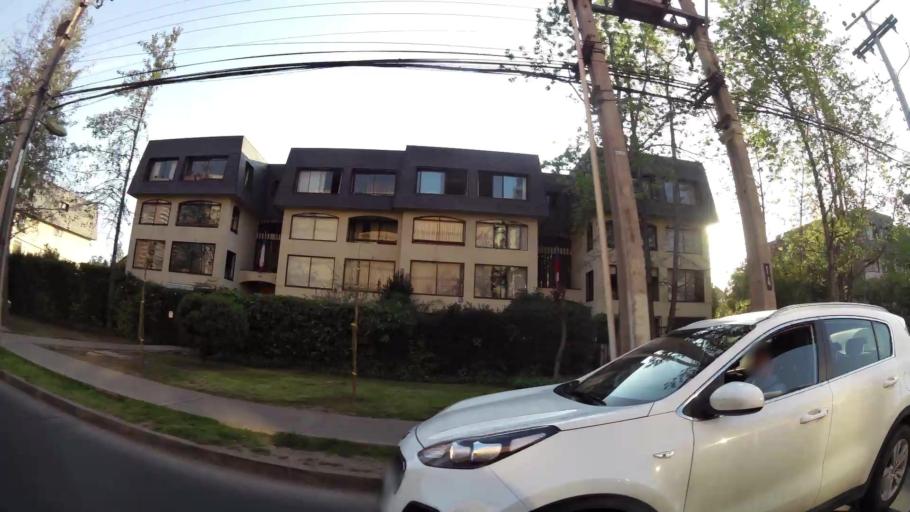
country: CL
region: Santiago Metropolitan
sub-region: Provincia de Santiago
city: Villa Presidente Frei, Nunoa, Santiago, Chile
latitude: -33.3909
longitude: -70.5470
